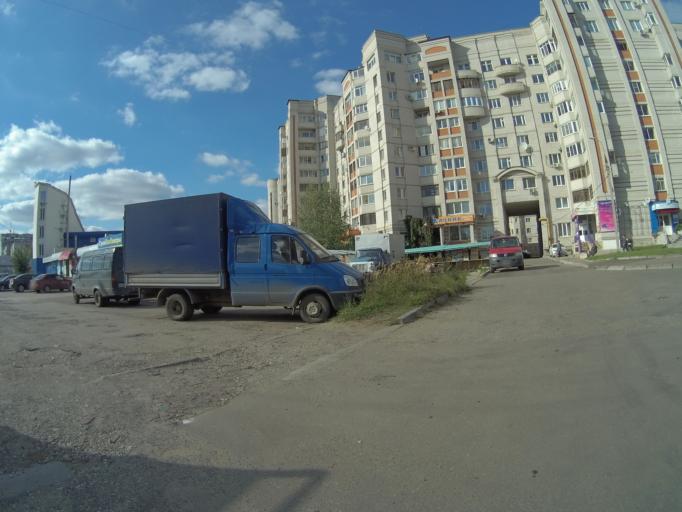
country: RU
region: Vladimir
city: Vladimir
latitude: 56.1051
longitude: 40.3485
